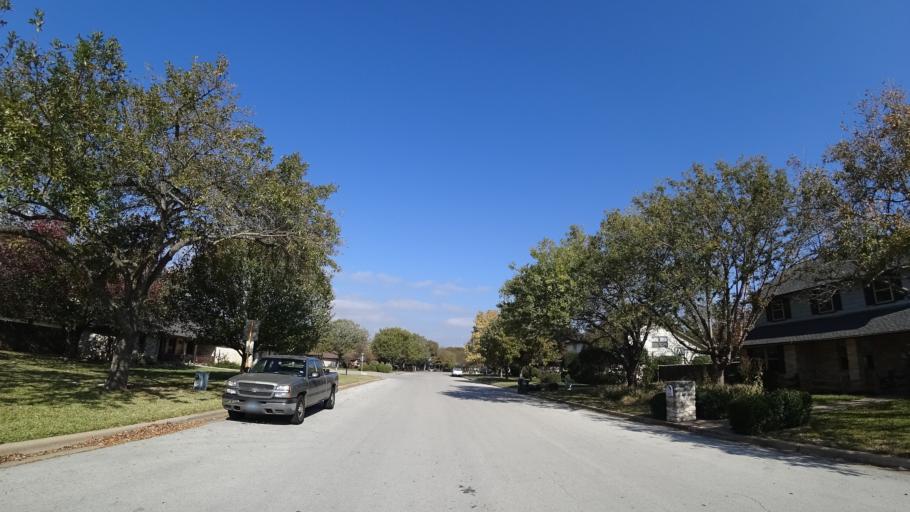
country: US
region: Texas
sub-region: Travis County
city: Shady Hollow
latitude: 30.1671
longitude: -97.8678
